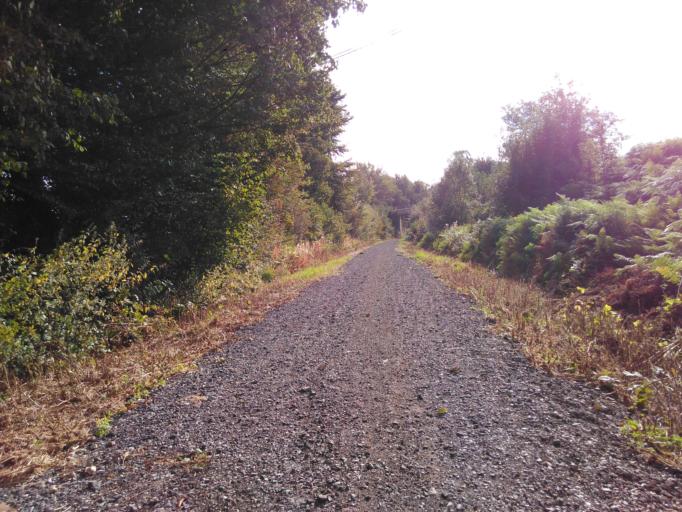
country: BE
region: Wallonia
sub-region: Province du Luxembourg
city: Neufchateau
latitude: 49.9189
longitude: 5.4170
